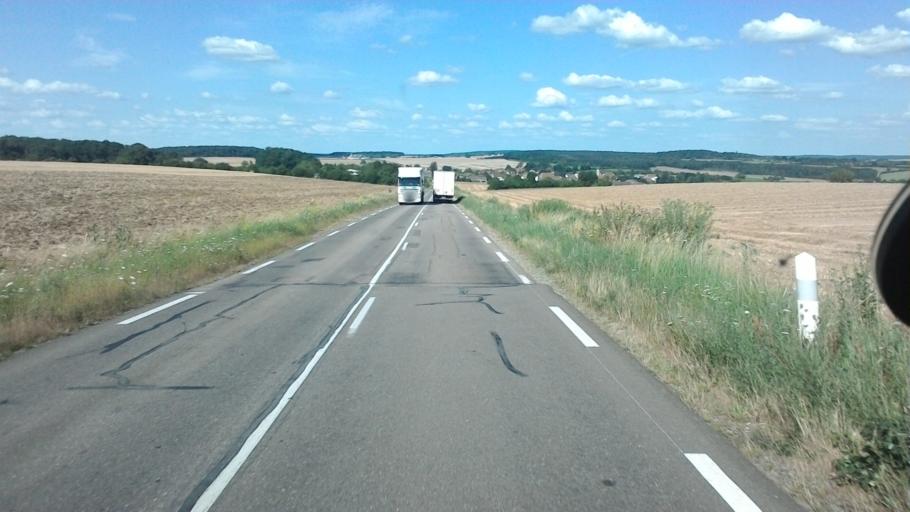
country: FR
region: Franche-Comte
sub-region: Departement de la Haute-Saone
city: Marnay
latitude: 47.3141
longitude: 5.6689
